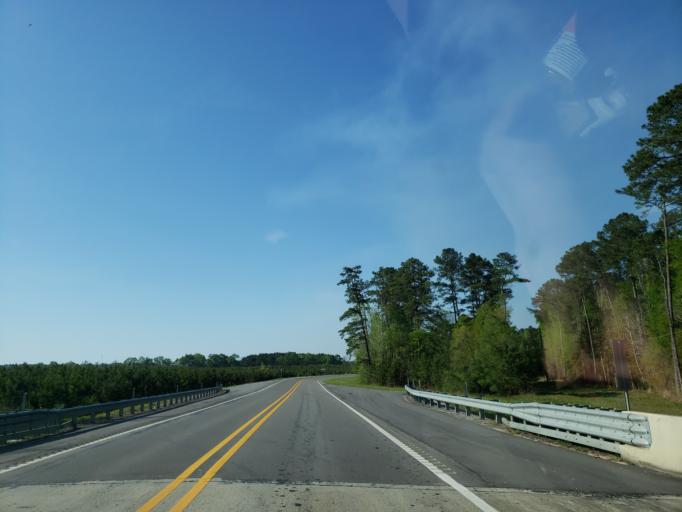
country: US
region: Mississippi
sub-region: Perry County
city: Richton
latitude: 31.3252
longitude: -88.9346
